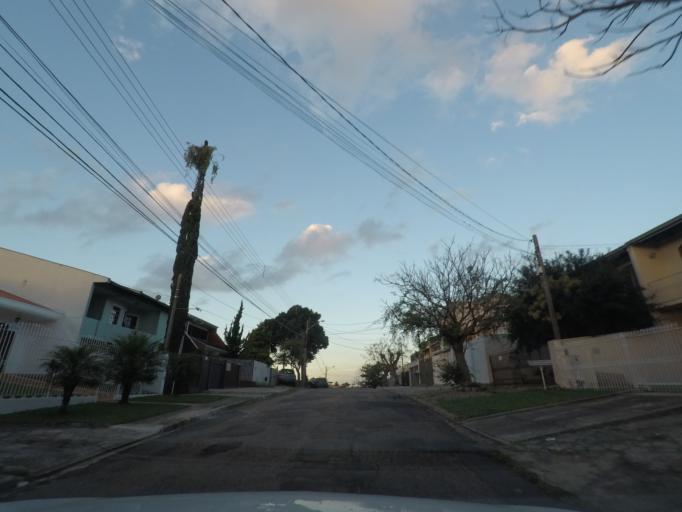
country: BR
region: Parana
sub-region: Sao Jose Dos Pinhais
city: Sao Jose dos Pinhais
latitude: -25.5008
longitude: -49.2627
